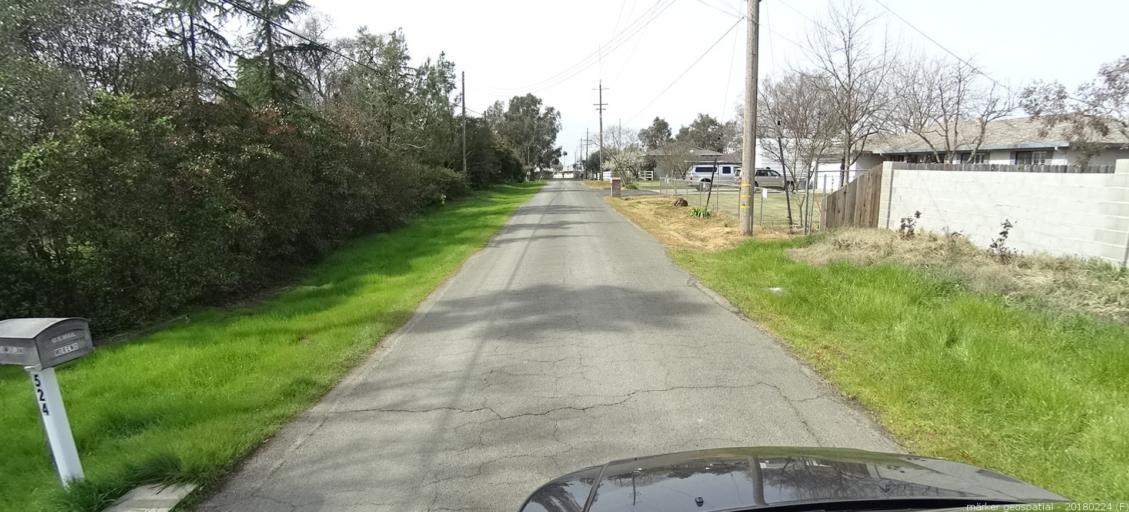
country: US
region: California
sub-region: Sacramento County
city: Elverta
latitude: 38.7100
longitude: -121.4739
